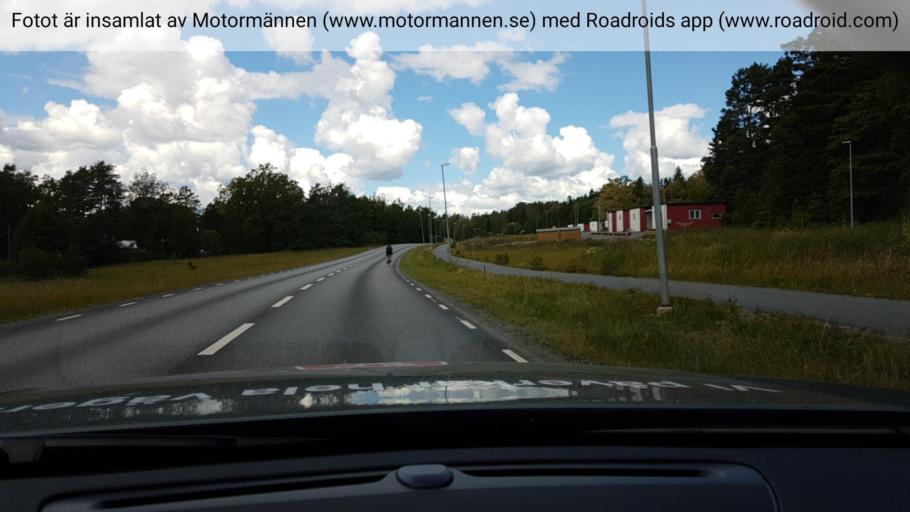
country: SE
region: Stockholm
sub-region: Varmdo Kommun
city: Hemmesta
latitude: 59.3289
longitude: 18.5005
